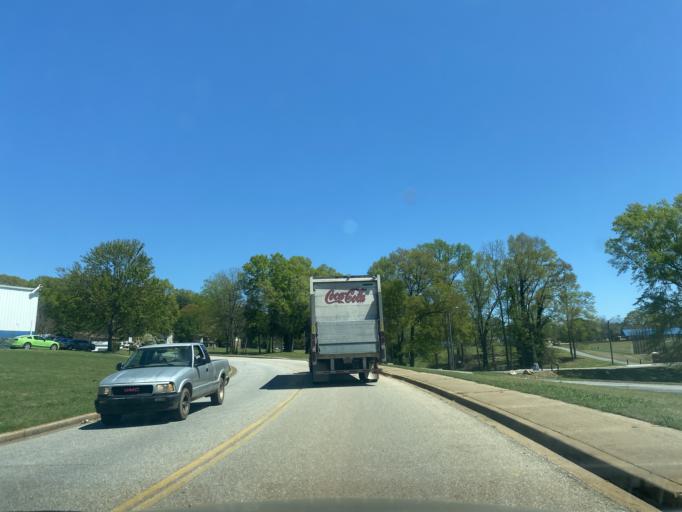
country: US
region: South Carolina
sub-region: Cherokee County
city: Gaffney
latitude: 35.0563
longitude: -81.6463
